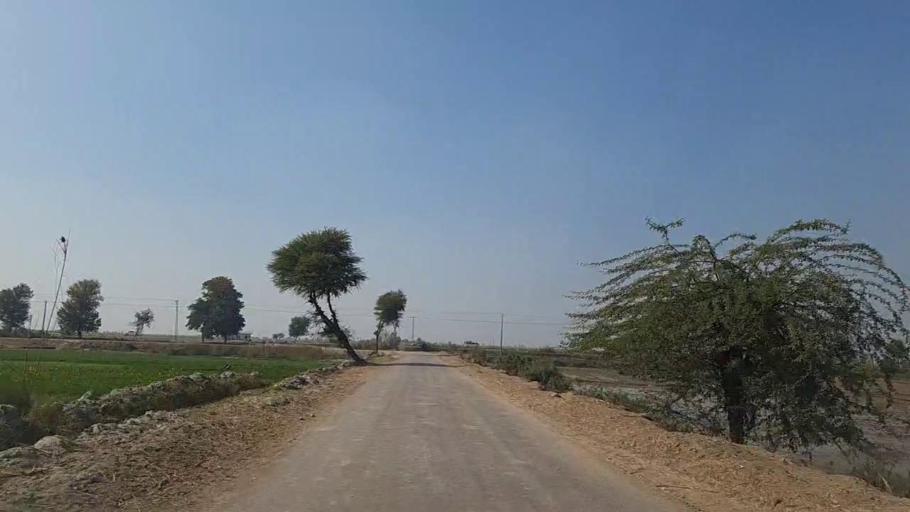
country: PK
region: Sindh
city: Daur
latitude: 26.5023
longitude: 68.3117
